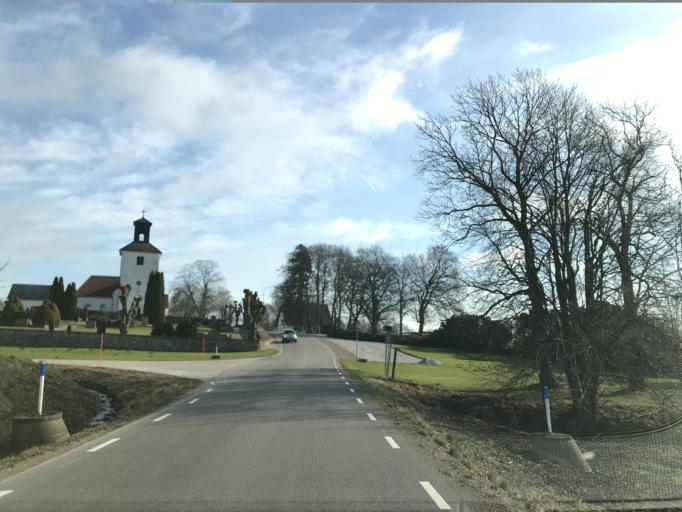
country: SE
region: Skane
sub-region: Hoors Kommun
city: Loberod
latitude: 55.7243
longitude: 13.5251
